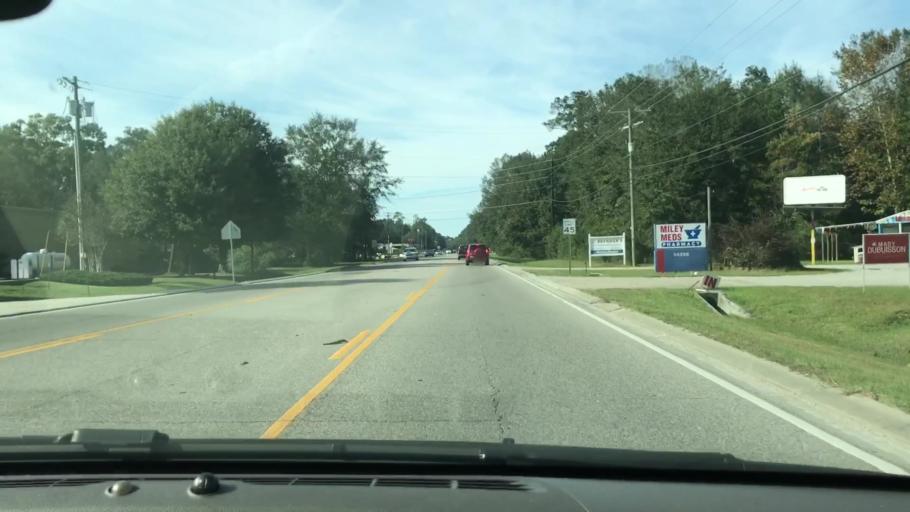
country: US
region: Louisiana
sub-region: Saint Tammany Parish
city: Pearl River
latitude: 30.3642
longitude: -89.7561
